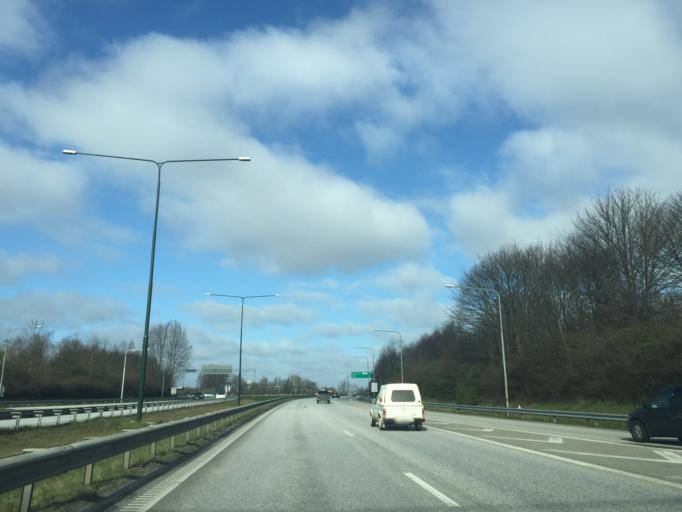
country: SE
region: Skane
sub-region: Malmo
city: Malmoe
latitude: 55.5643
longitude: 13.0075
